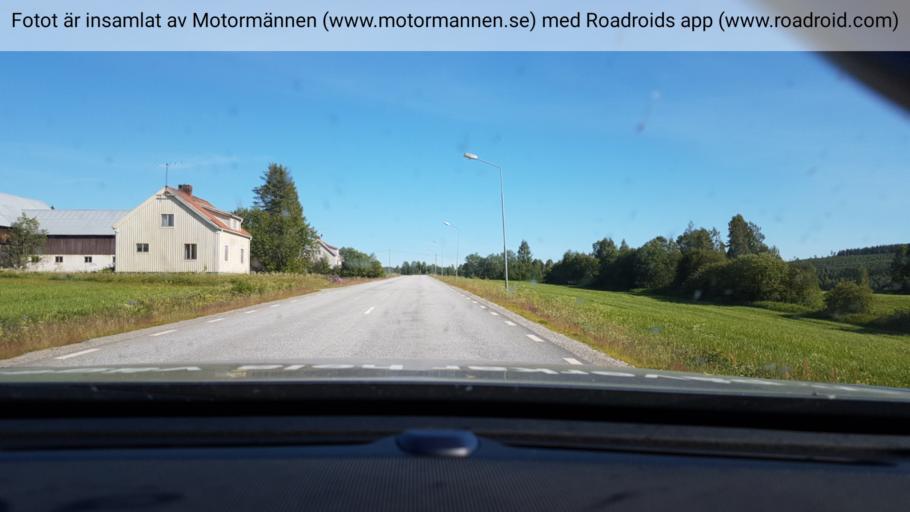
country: SE
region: Vaesterbotten
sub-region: Vindelns Kommun
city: Vindeln
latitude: 64.1710
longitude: 19.4888
